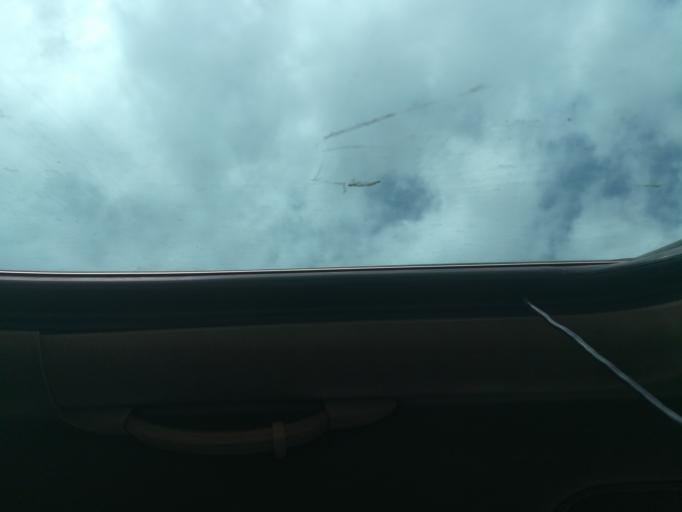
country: NG
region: Lagos
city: Lagos
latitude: 6.4120
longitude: 3.4136
